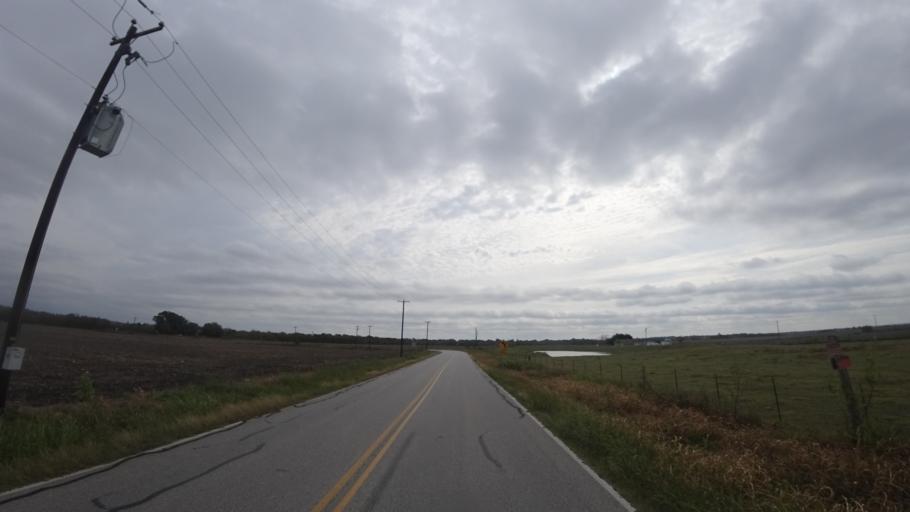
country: US
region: Texas
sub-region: Travis County
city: Manor
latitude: 30.4016
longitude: -97.5475
